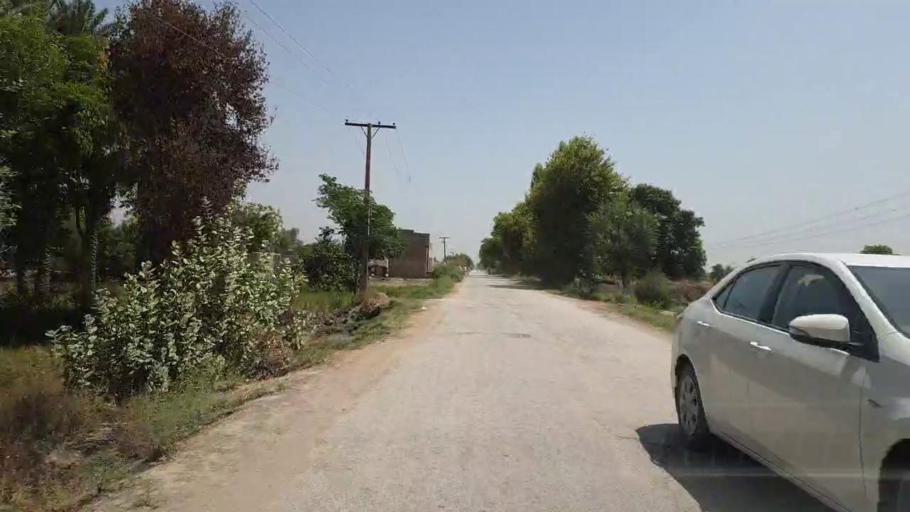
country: PK
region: Sindh
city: Adilpur
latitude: 27.8325
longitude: 69.2567
